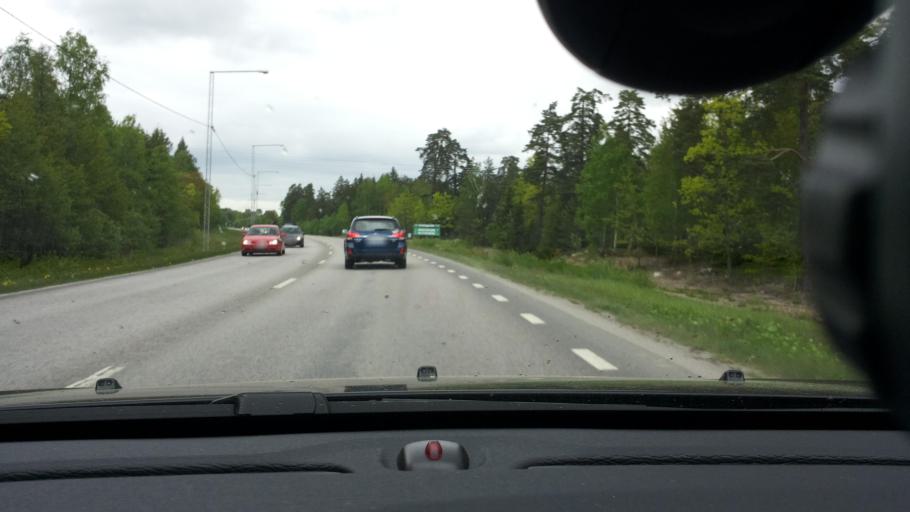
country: SE
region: Stockholm
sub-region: Taby Kommun
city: Taby
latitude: 59.4764
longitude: 18.1212
